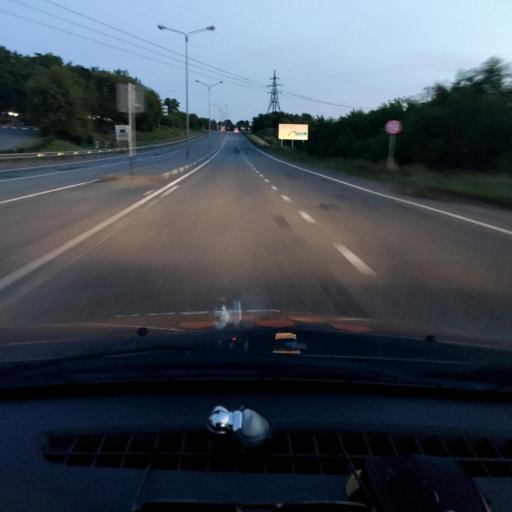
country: RU
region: Belgorod
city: Gubkin
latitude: 51.2815
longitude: 37.5957
